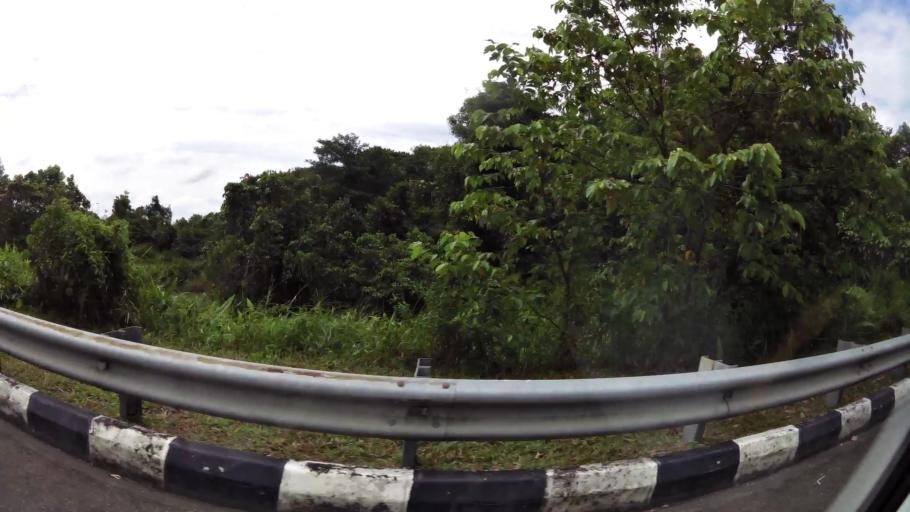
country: BN
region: Brunei and Muara
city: Bandar Seri Begawan
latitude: 4.9212
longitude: 114.9132
